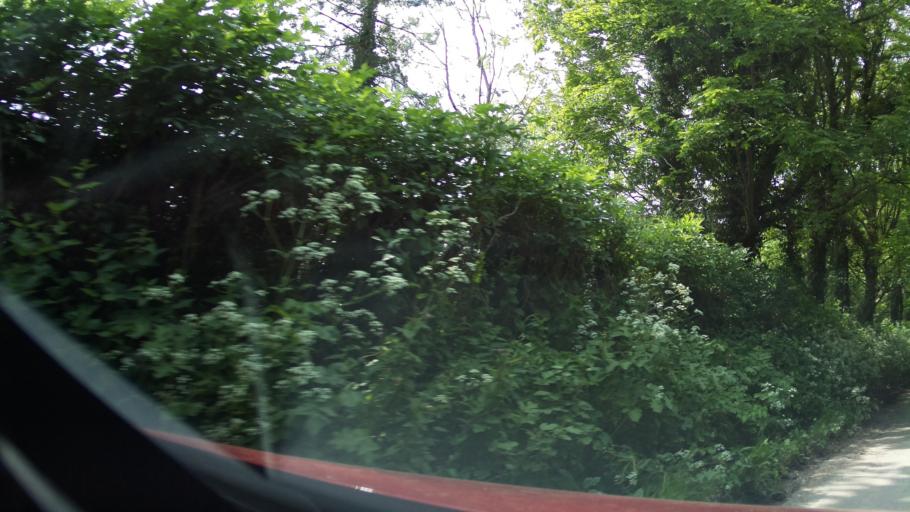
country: GB
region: England
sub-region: South Gloucestershire
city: Horton
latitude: 51.5441
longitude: -2.3500
